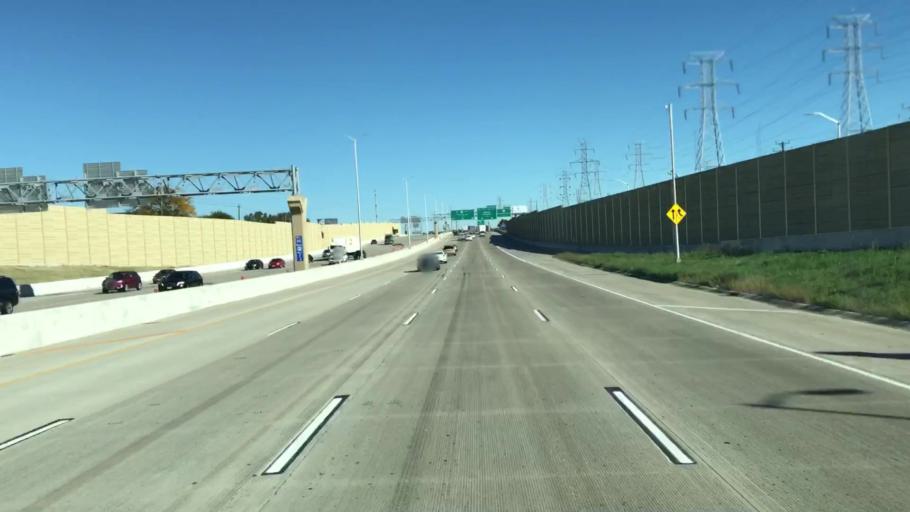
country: US
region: Wisconsin
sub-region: Milwaukee County
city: West Allis
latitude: 43.0049
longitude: -88.0376
